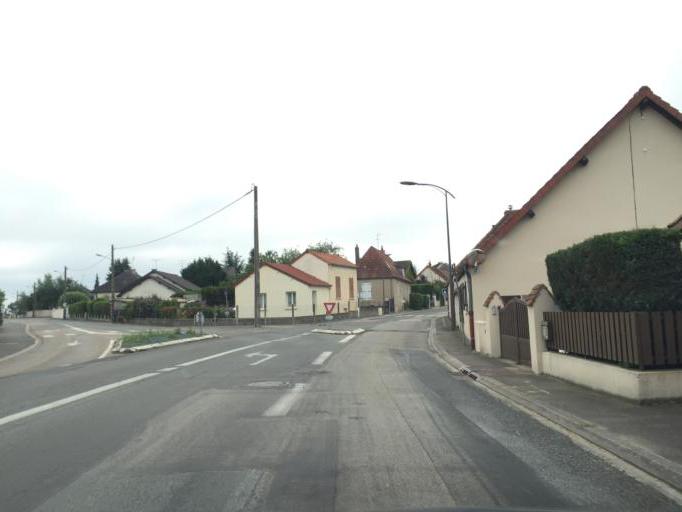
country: FR
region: Auvergne
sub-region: Departement de l'Allier
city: Avermes
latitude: 46.5863
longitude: 3.3115
